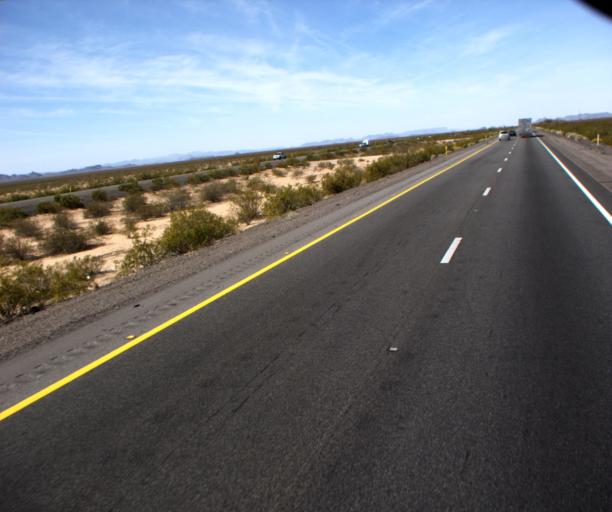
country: US
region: Arizona
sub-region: La Paz County
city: Salome
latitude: 33.5799
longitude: -113.4235
